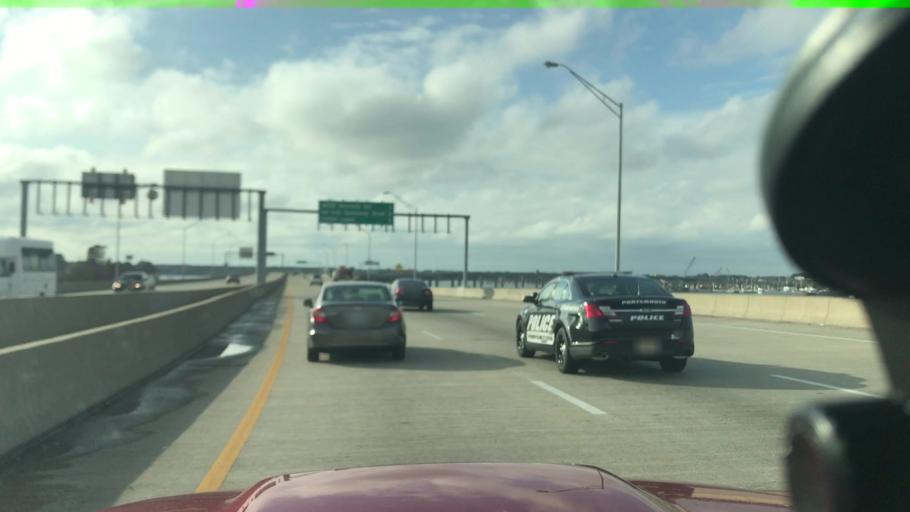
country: US
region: Virginia
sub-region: City of Portsmouth
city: Portsmouth
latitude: 36.8552
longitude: -76.3356
